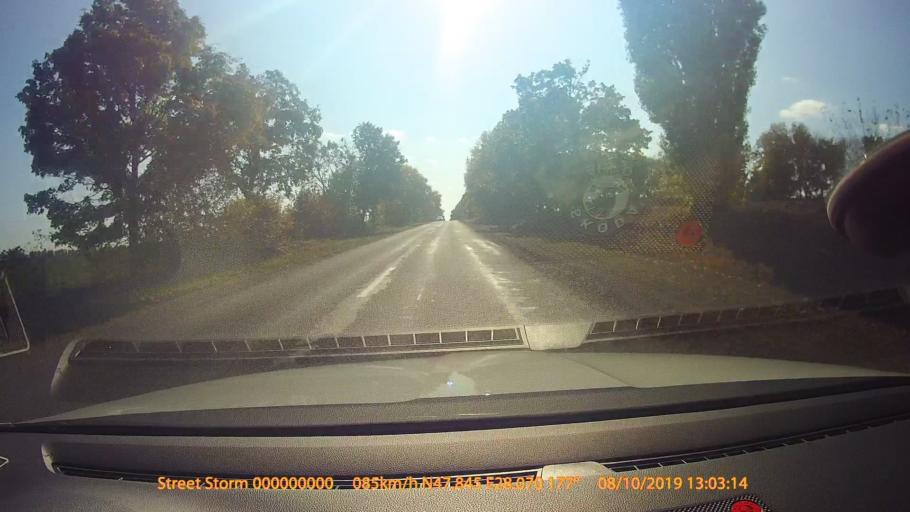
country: MD
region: Singerei
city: Biruinta
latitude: 47.8449
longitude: 28.0696
